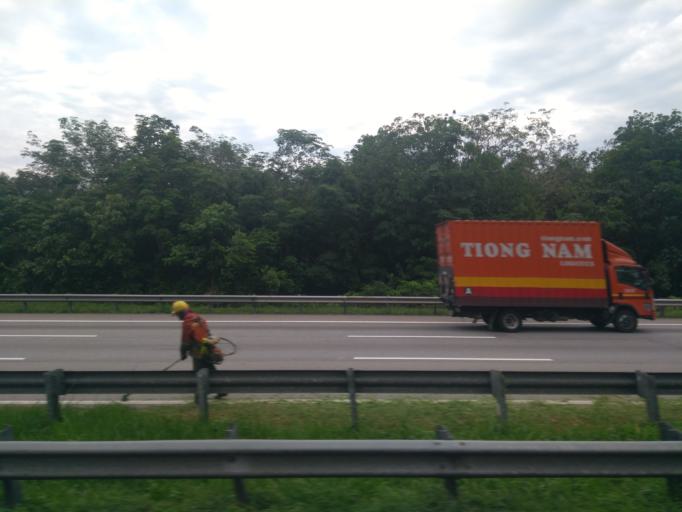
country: MY
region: Melaka
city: Alor Gajah
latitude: 2.4158
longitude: 102.2169
